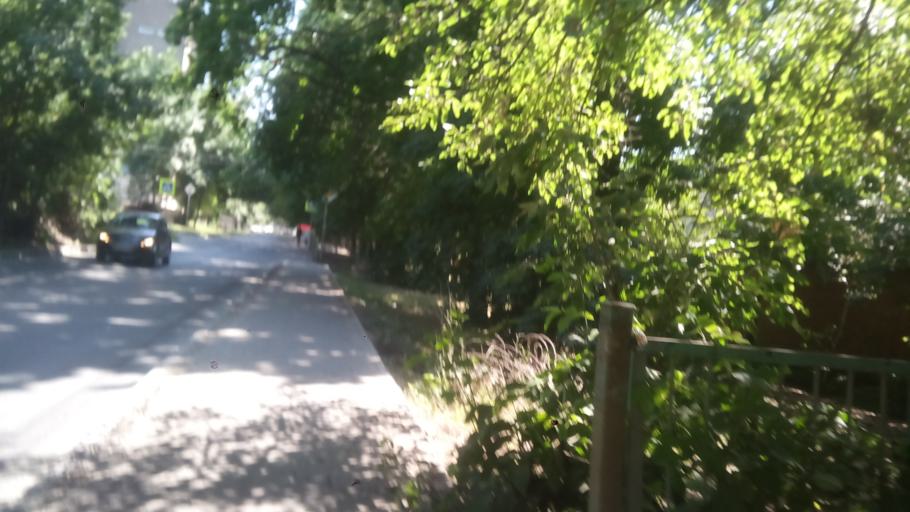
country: RU
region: Rostov
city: Rostov-na-Donu
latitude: 47.2204
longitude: 39.6267
